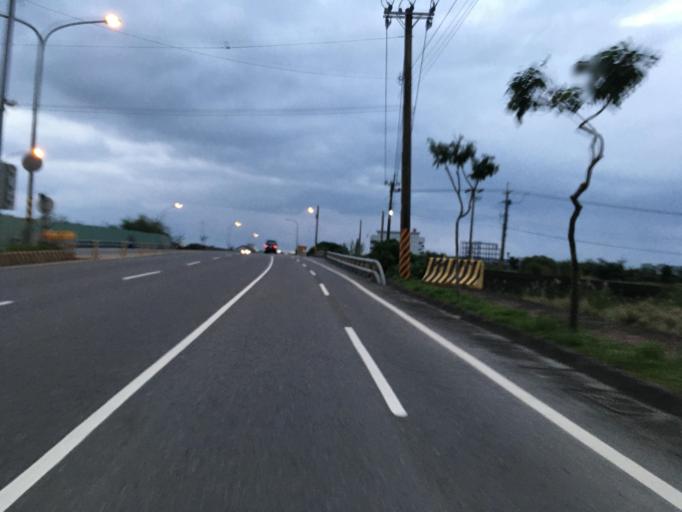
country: TW
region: Taiwan
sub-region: Yilan
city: Yilan
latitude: 24.6300
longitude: 121.8320
